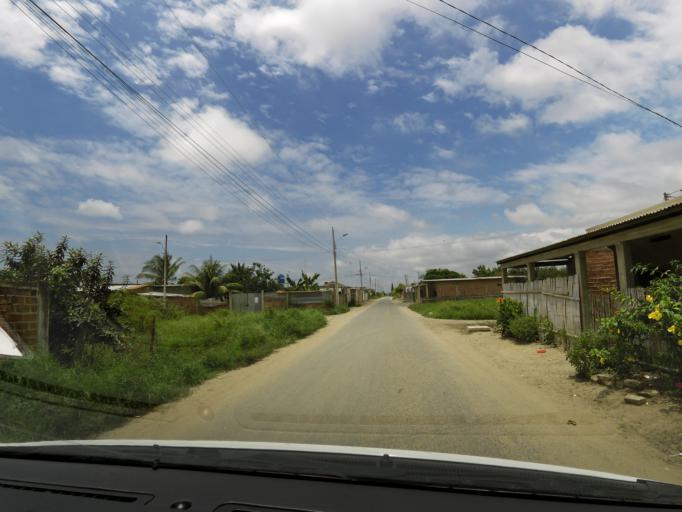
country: EC
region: El Oro
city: Huaquillas
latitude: -3.4860
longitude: -80.2099
